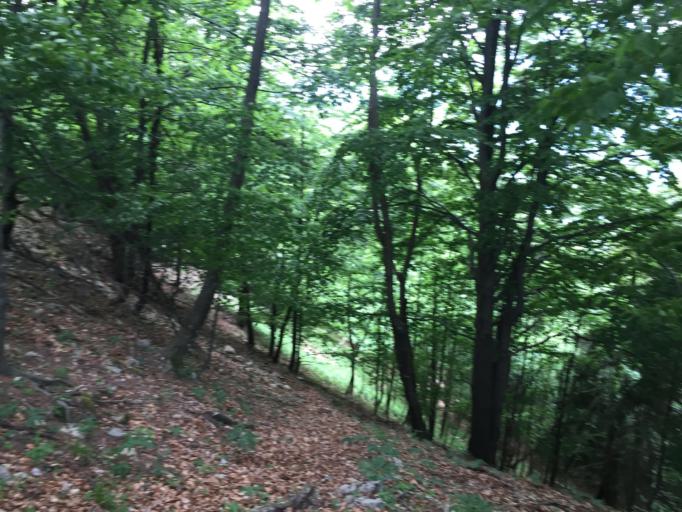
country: SI
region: Tolmin
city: Tolmin
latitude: 46.1739
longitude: 13.8550
